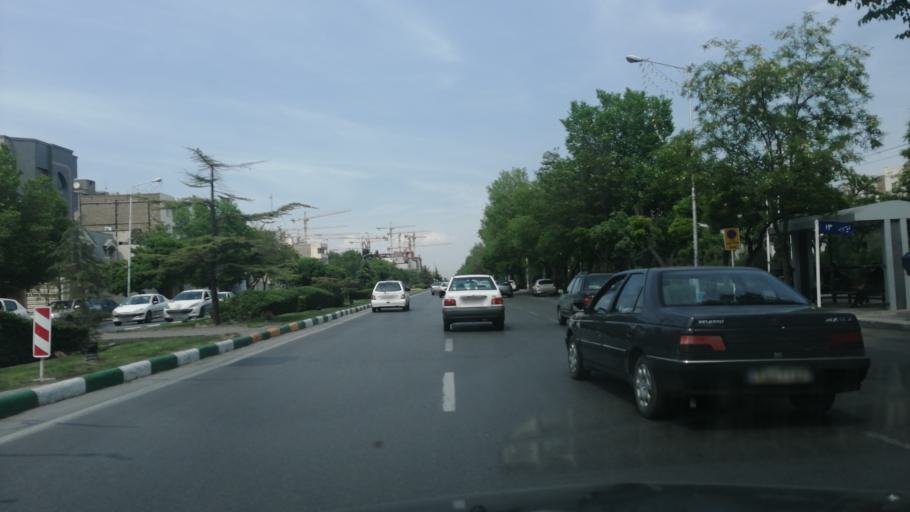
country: IR
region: Razavi Khorasan
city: Mashhad
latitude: 36.3104
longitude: 59.5555
